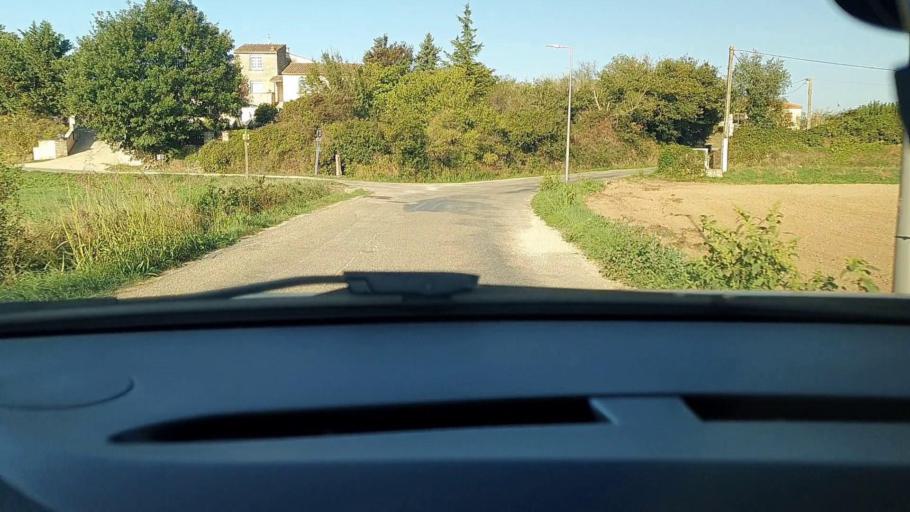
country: FR
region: Languedoc-Roussillon
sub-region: Departement du Gard
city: Barjac
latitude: 44.2575
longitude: 4.2899
